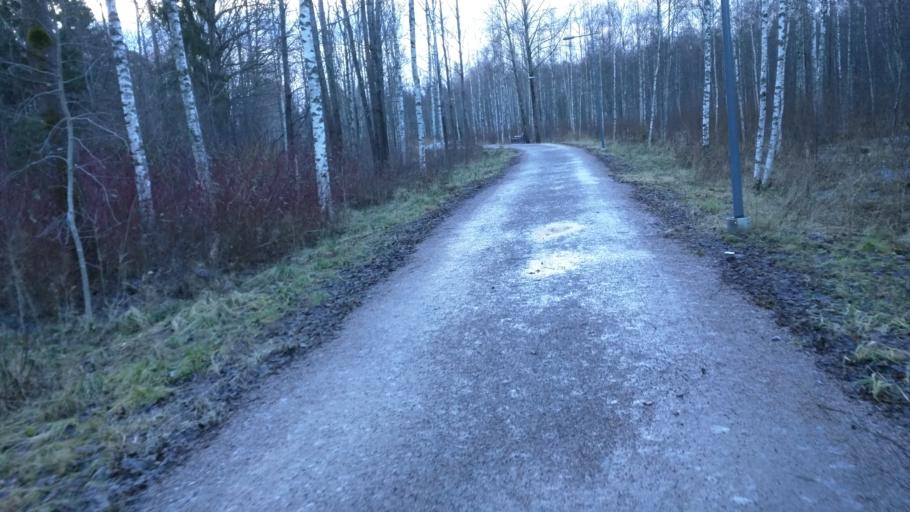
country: FI
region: Uusimaa
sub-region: Helsinki
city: Kauniainen
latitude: 60.2404
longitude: 24.7336
